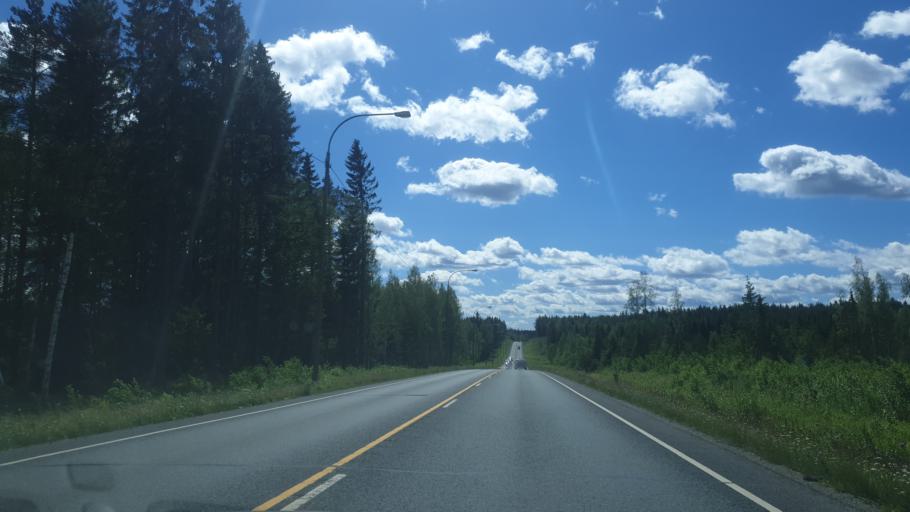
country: FI
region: Northern Savo
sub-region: Varkaus
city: Leppaevirta
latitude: 62.6187
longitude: 27.6224
